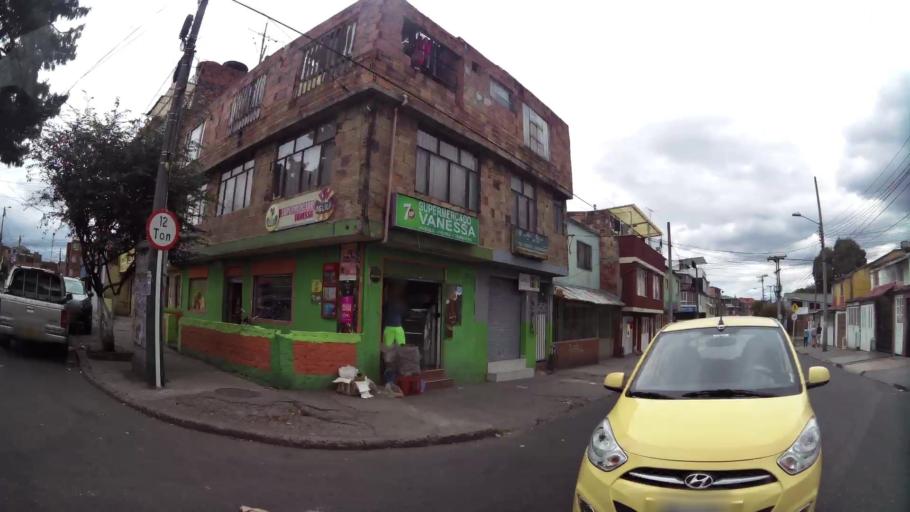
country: CO
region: Bogota D.C.
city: Bogota
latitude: 4.6202
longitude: -74.1069
